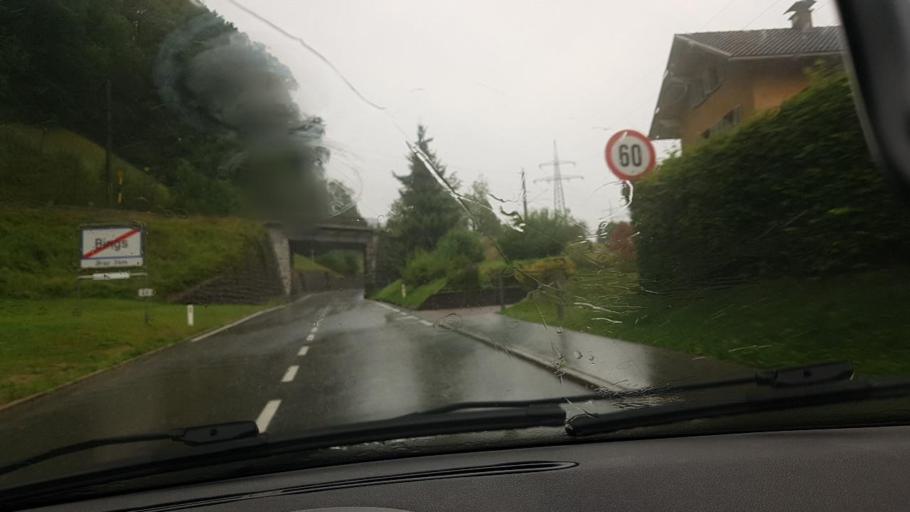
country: AT
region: Vorarlberg
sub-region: Politischer Bezirk Bludenz
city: Stallehr
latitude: 47.1447
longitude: 9.8649
